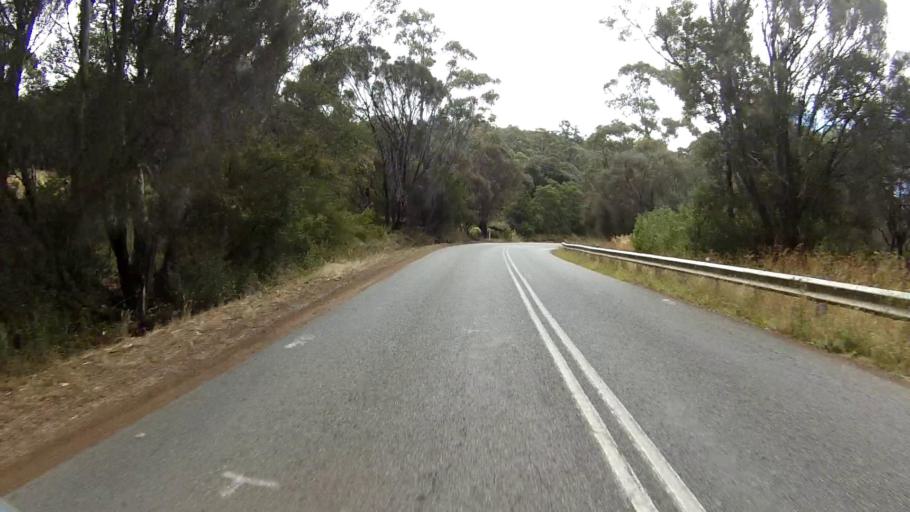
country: AU
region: Tasmania
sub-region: Sorell
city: Sorell
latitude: -42.2400
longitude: 148.0122
